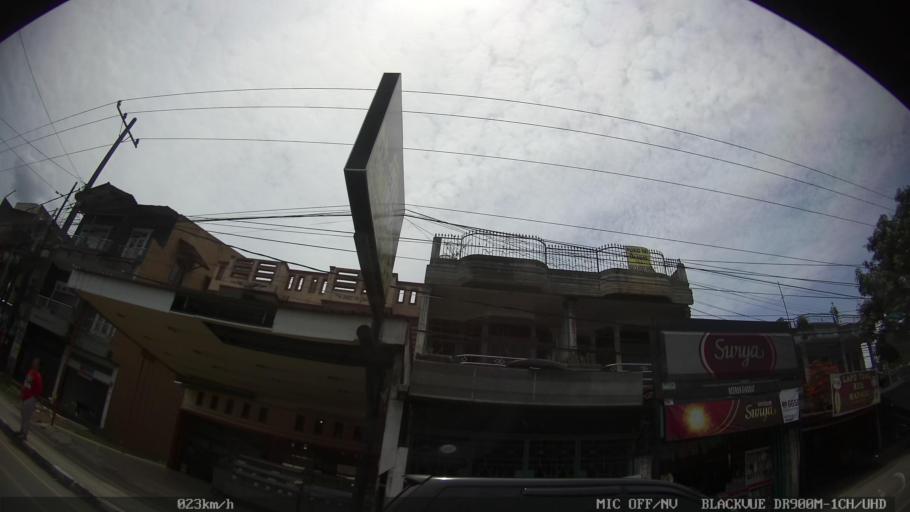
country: ID
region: North Sumatra
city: Sunggal
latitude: 3.5441
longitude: 98.6248
